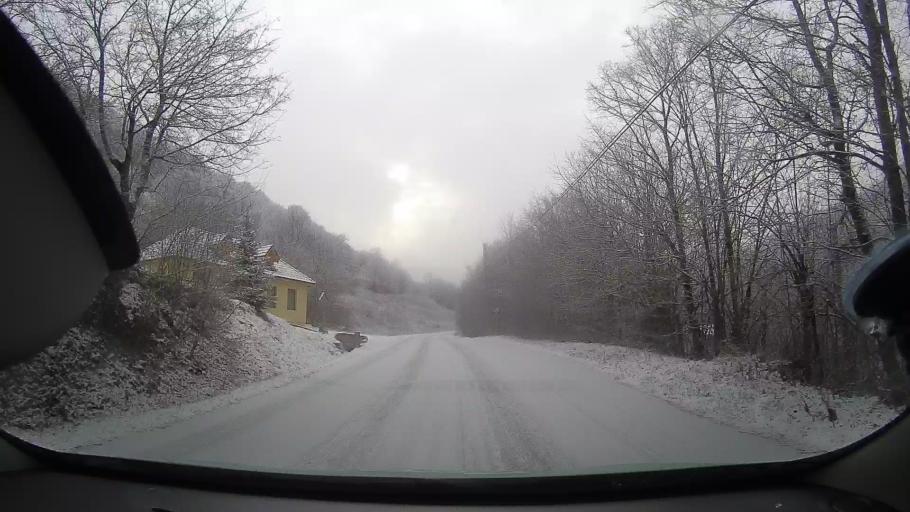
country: RO
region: Alba
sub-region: Comuna Rimetea
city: Rimetea
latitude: 46.4894
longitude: 23.5804
